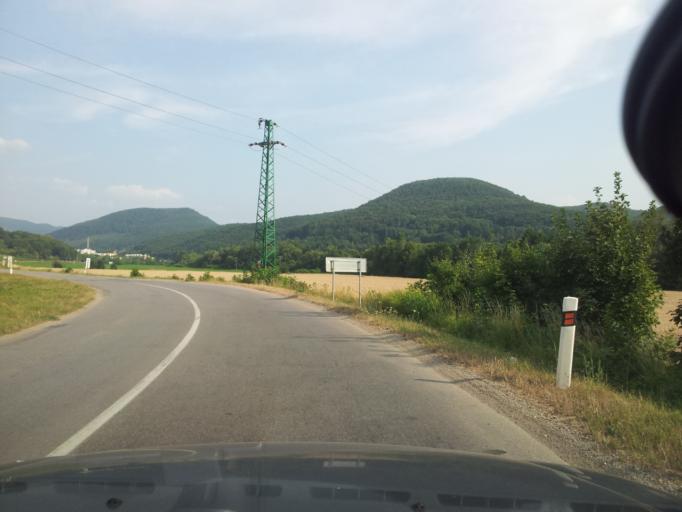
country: SK
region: Trenciansky
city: Nova Dubnica
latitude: 48.9223
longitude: 18.1425
